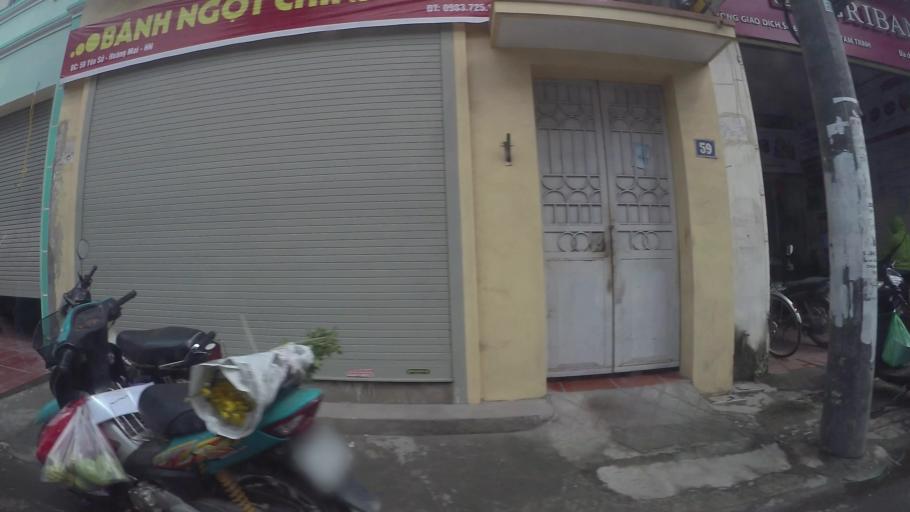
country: VN
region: Ha Noi
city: Van Dien
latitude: 20.9667
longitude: 105.8699
